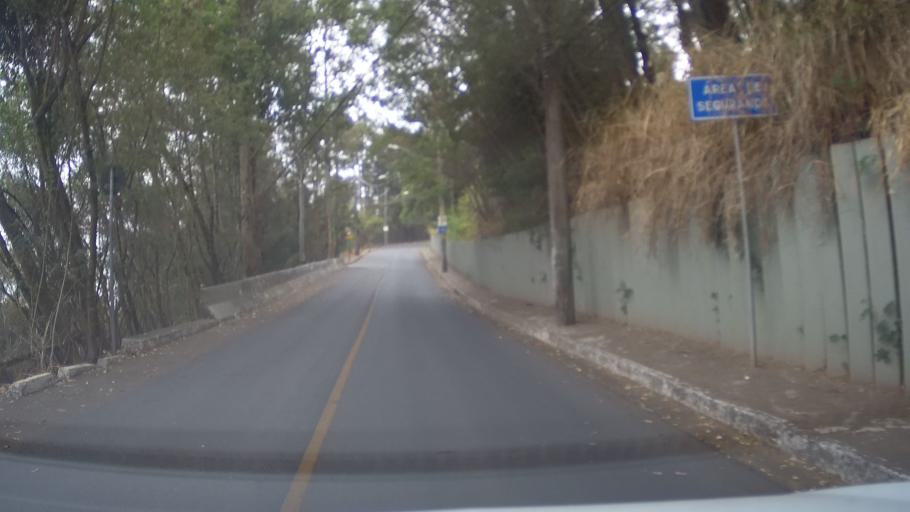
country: BR
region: Minas Gerais
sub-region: Belo Horizonte
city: Belo Horizonte
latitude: -19.9546
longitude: -43.9132
